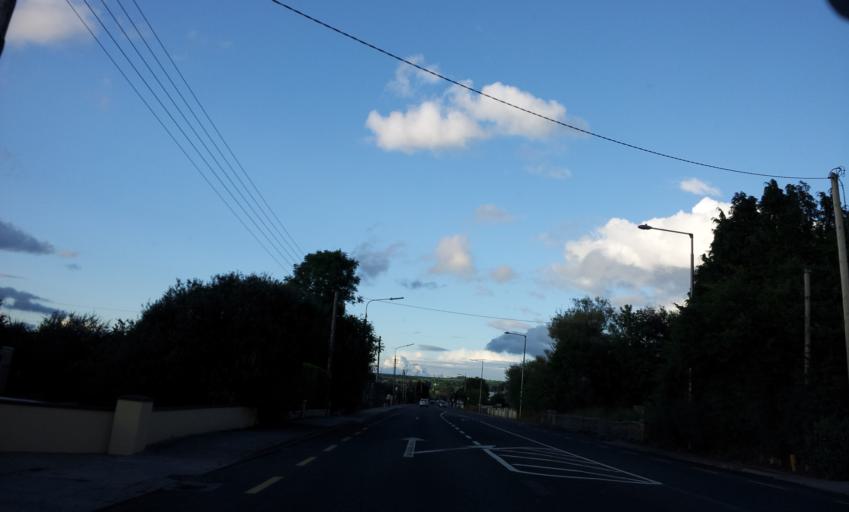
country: IE
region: Munster
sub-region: County Limerick
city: Abbeyfeale
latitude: 52.3763
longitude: -9.3080
